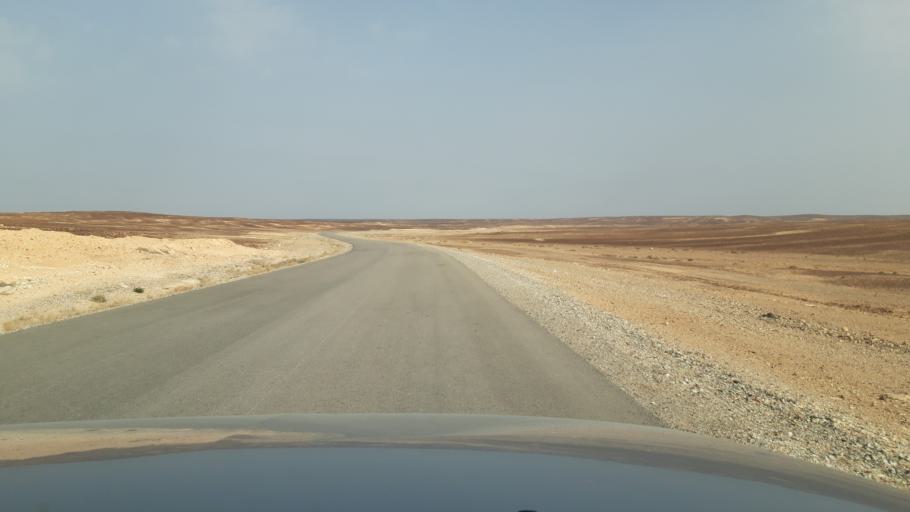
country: JO
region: Amman
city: Al Azraq ash Shamali
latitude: 31.2775
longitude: 36.5824
